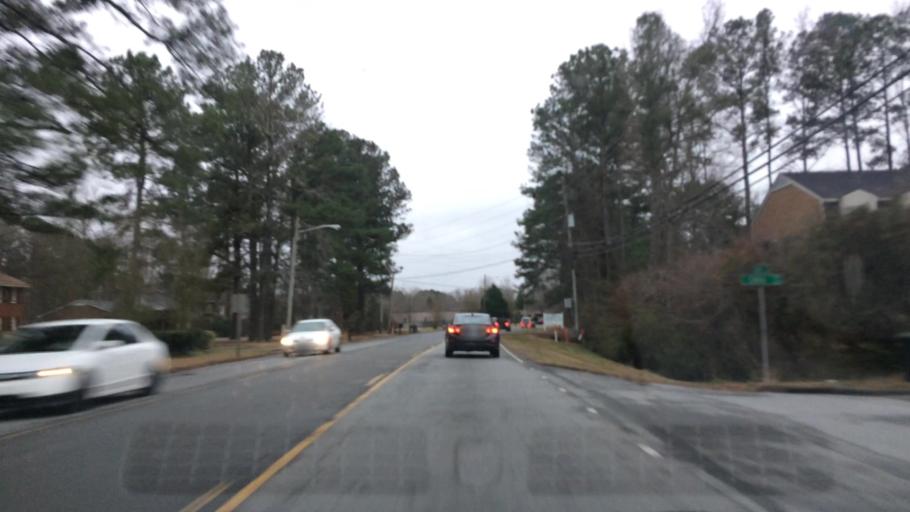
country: US
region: North Carolina
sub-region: Pitt County
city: Summerfield
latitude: 35.5689
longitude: -77.3829
